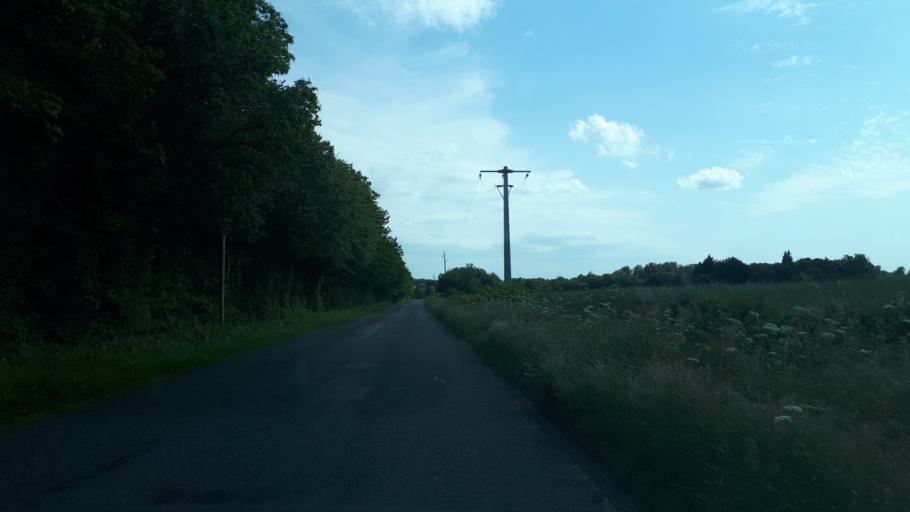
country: FR
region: Centre
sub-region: Departement du Cher
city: Henrichemont
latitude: 47.3818
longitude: 2.5975
